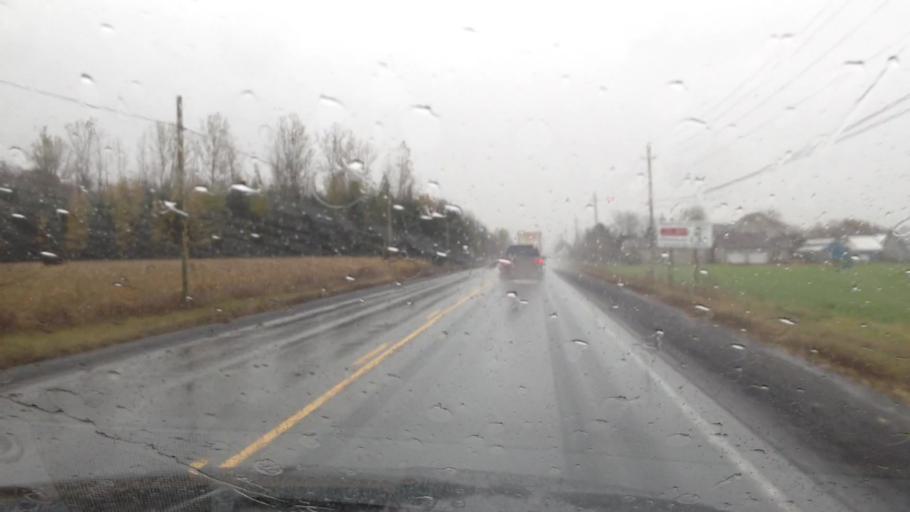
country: CA
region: Ontario
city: Bourget
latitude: 45.2772
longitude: -75.3150
